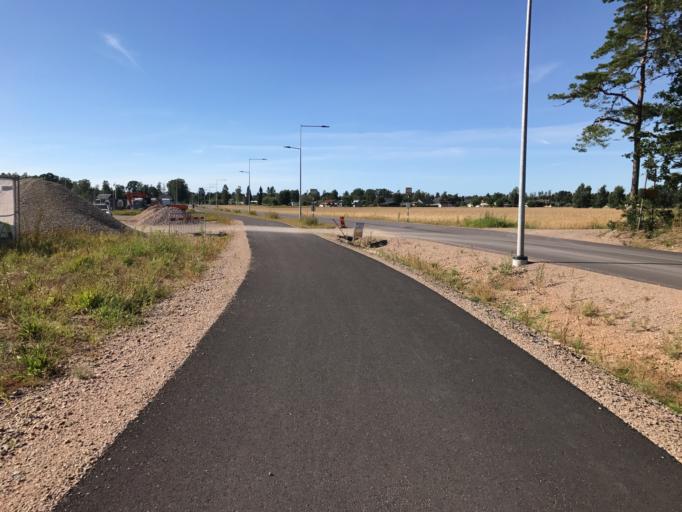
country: SE
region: Skane
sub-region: Bastads Kommun
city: Bastad
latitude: 56.4337
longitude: 12.9077
